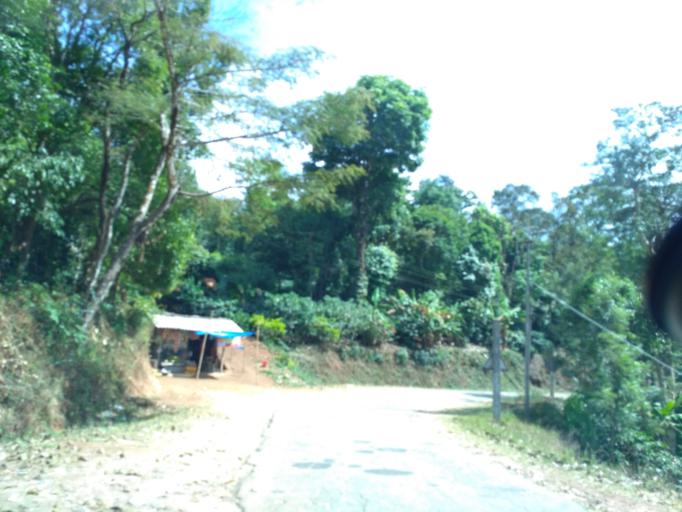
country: IN
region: Karnataka
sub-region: Kodagu
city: Madikeri
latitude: 12.4170
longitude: 75.7113
